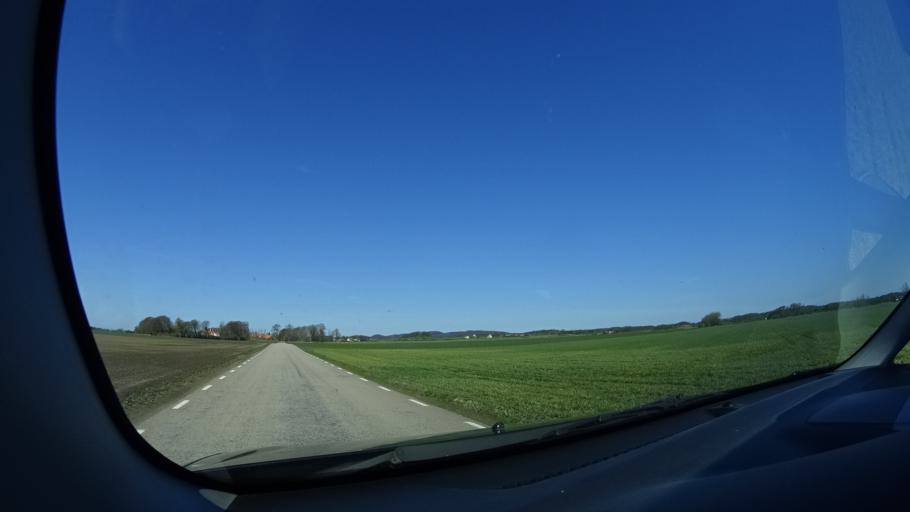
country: SE
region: Skane
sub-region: Hoganas Kommun
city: Hoganas
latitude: 56.2396
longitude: 12.5833
